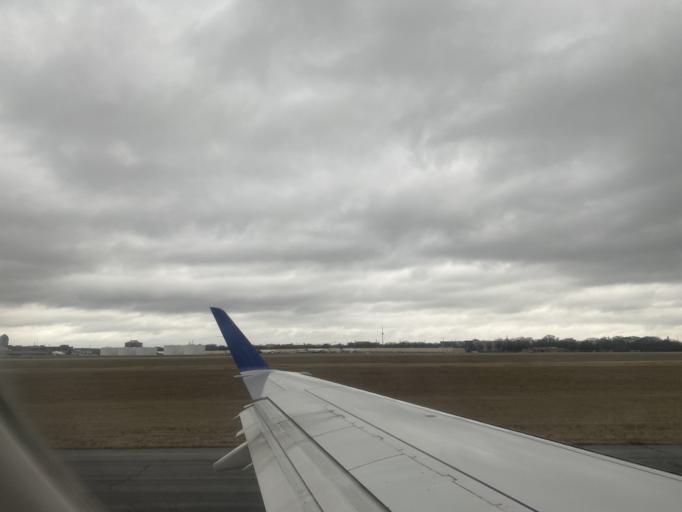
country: US
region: Georgia
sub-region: Fulton County
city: Hapeville
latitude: 33.6453
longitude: -84.4133
